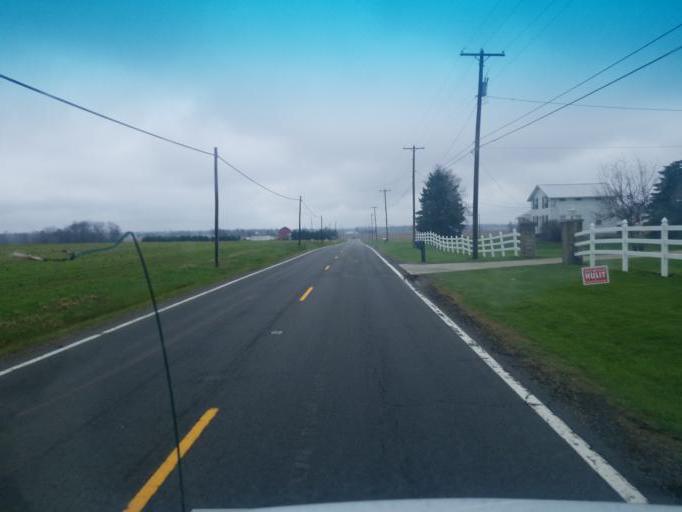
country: US
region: Ohio
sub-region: Huron County
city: Plymouth
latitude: 40.9470
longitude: -82.6671
